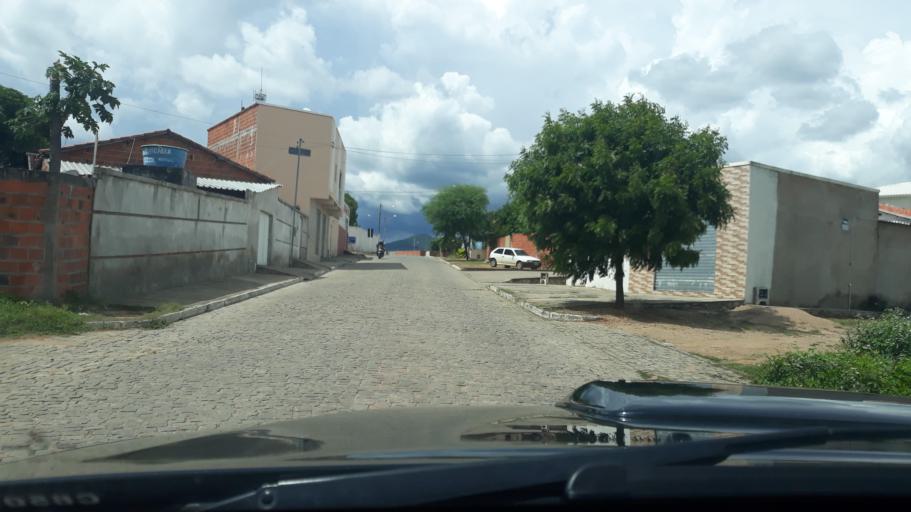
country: BR
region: Bahia
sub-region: Riacho De Santana
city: Riacho de Santana
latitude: -13.9115
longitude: -42.8433
